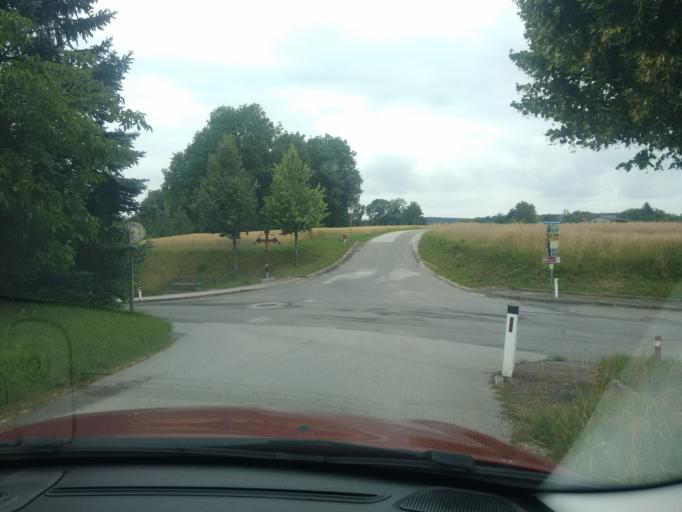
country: AT
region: Upper Austria
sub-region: Politischer Bezirk Steyr-Land
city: Bad Hall
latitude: 48.0405
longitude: 14.2267
